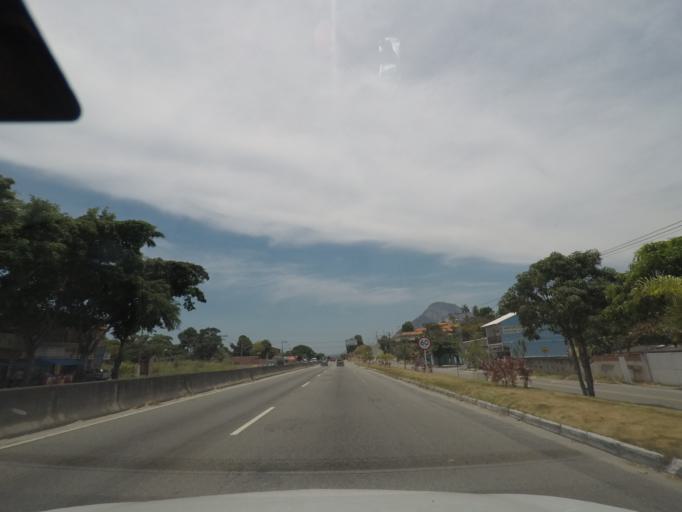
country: BR
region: Rio de Janeiro
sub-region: Marica
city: Marica
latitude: -22.9312
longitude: -42.8788
